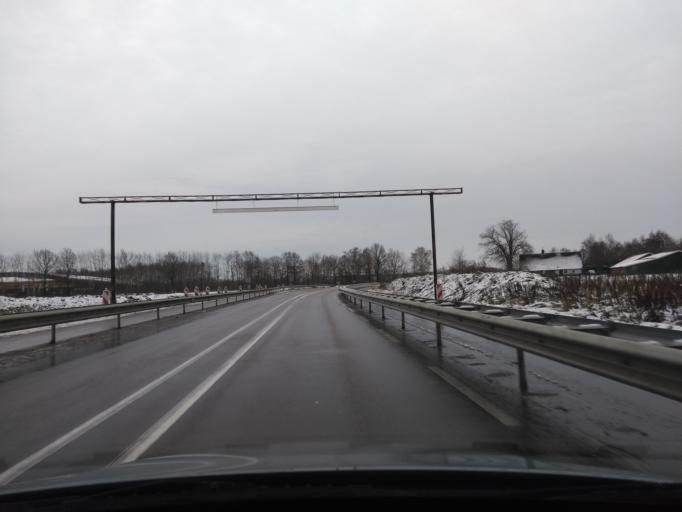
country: NL
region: Overijssel
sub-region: Gemeente Haaksbergen
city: Haaksbergen
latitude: 52.1801
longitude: 6.7386
